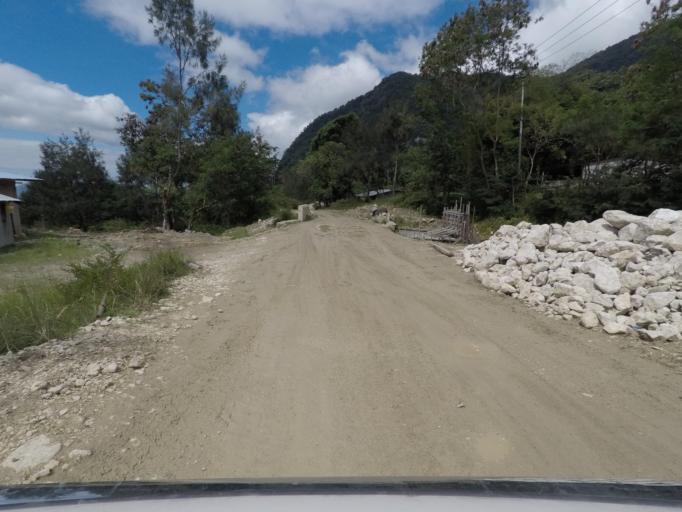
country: TL
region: Baucau
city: Venilale
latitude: -8.7097
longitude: 126.3639
